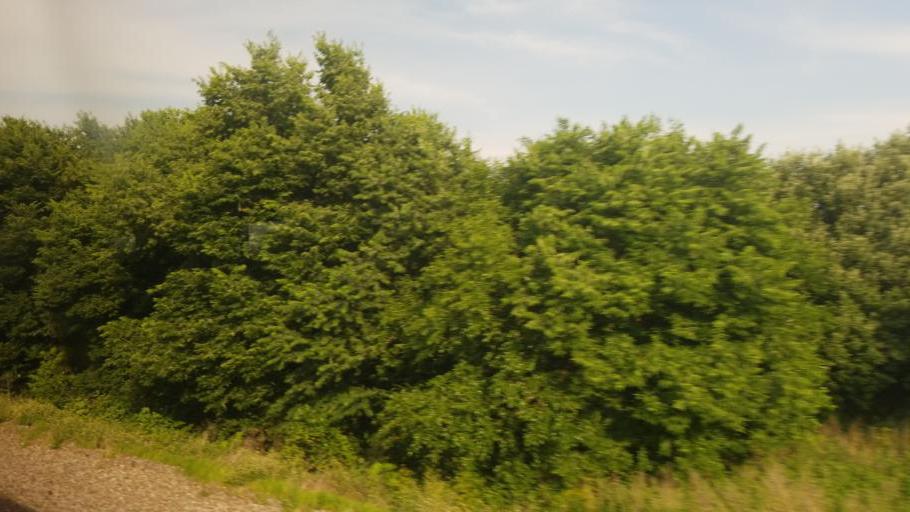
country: US
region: Illinois
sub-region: Kendall County
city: Lynwood
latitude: 41.6986
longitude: -88.3778
